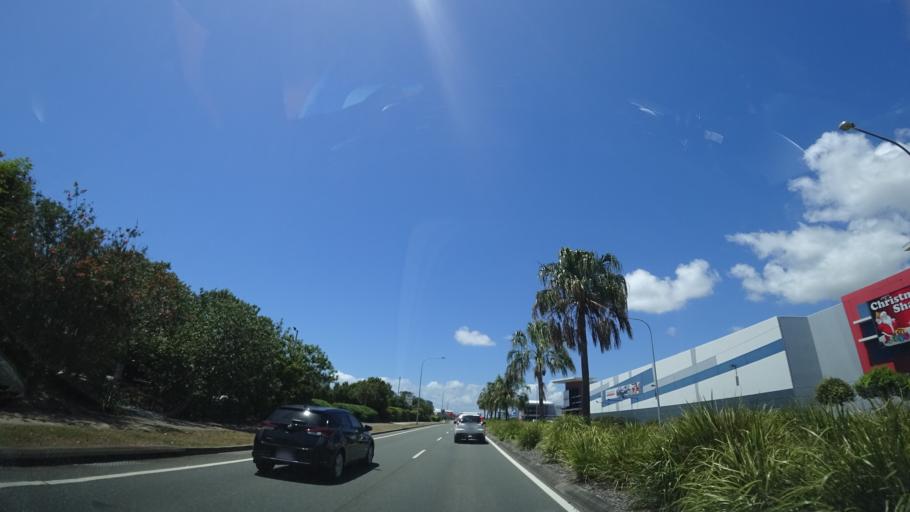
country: AU
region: Queensland
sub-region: Sunshine Coast
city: Mooloolaba
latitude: -26.7335
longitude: 153.1205
